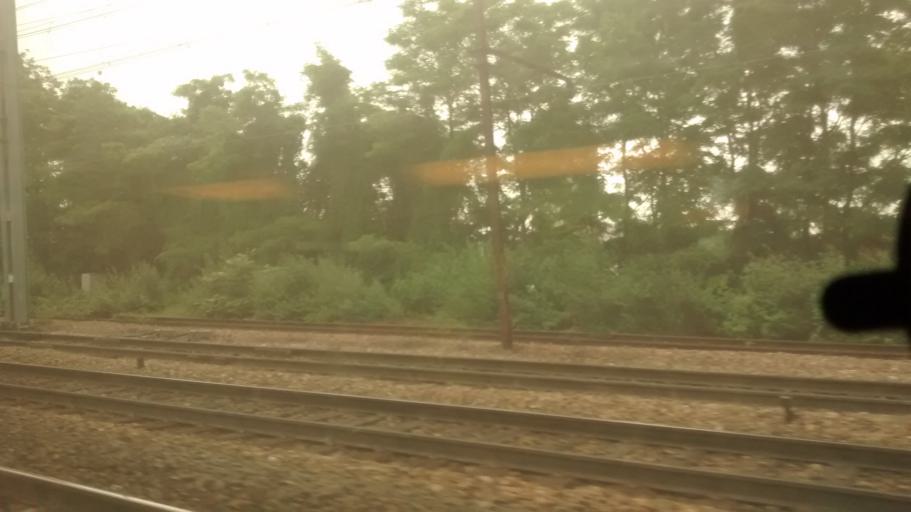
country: FR
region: Ile-de-France
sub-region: Departement du Val-de-Marne
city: Valenton
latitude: 48.7565
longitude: 2.4460
